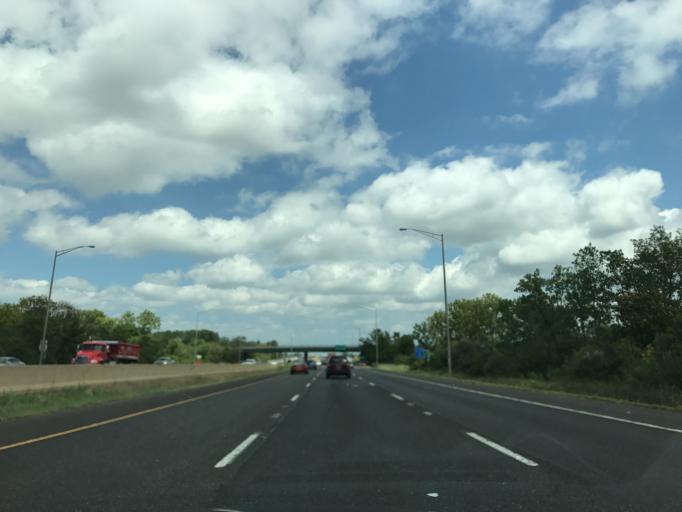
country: US
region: Illinois
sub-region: Cook County
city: Country Club Hills
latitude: 41.5804
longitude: -87.7368
